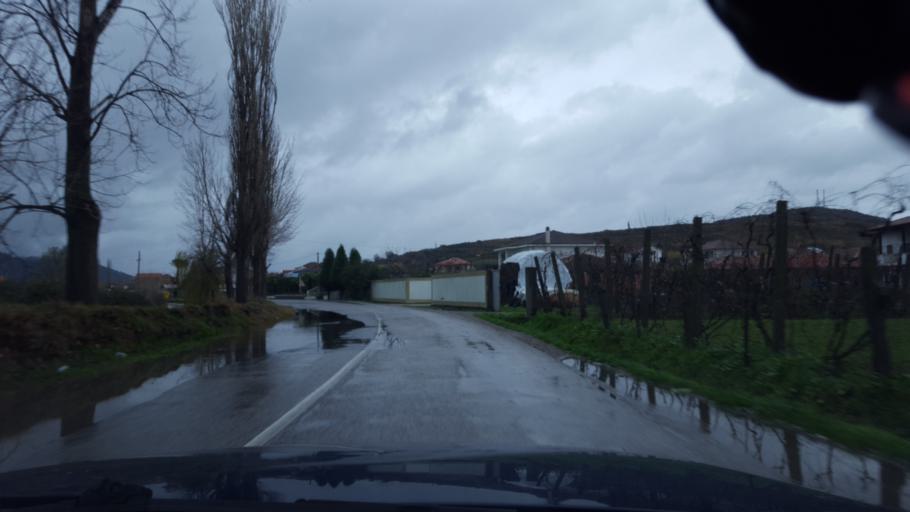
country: AL
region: Shkoder
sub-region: Rrethi i Shkodres
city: Berdica e Madhe
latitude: 42.0077
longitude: 19.4805
